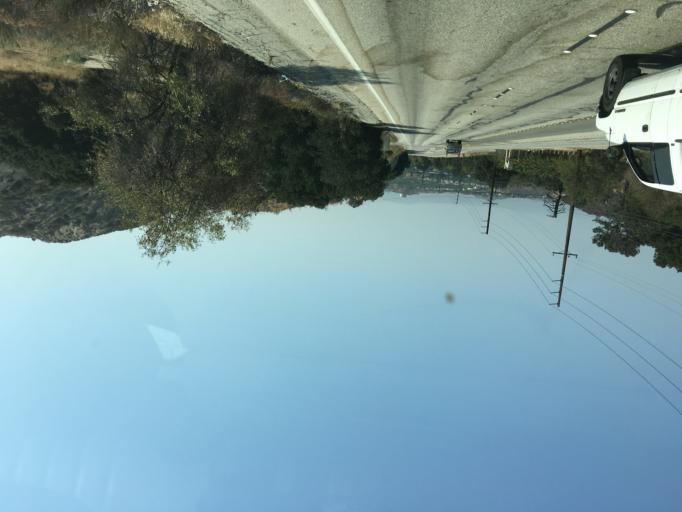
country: US
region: California
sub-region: Los Angeles County
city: Santa Clarita
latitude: 34.3546
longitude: -118.5081
